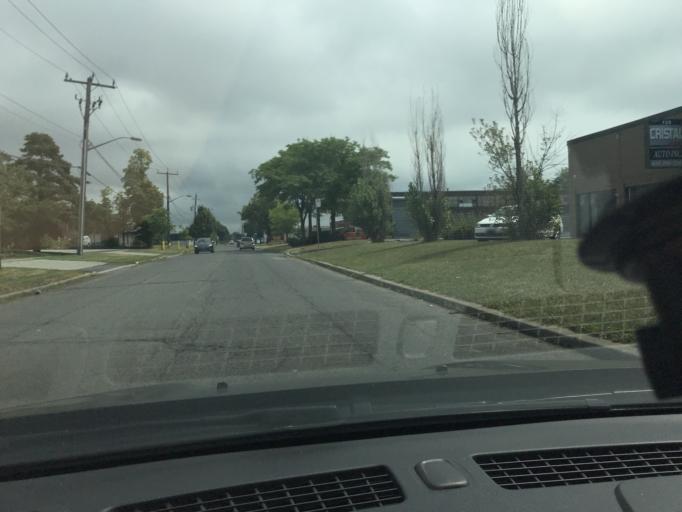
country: CA
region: Ontario
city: Concord
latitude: 43.7569
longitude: -79.4867
